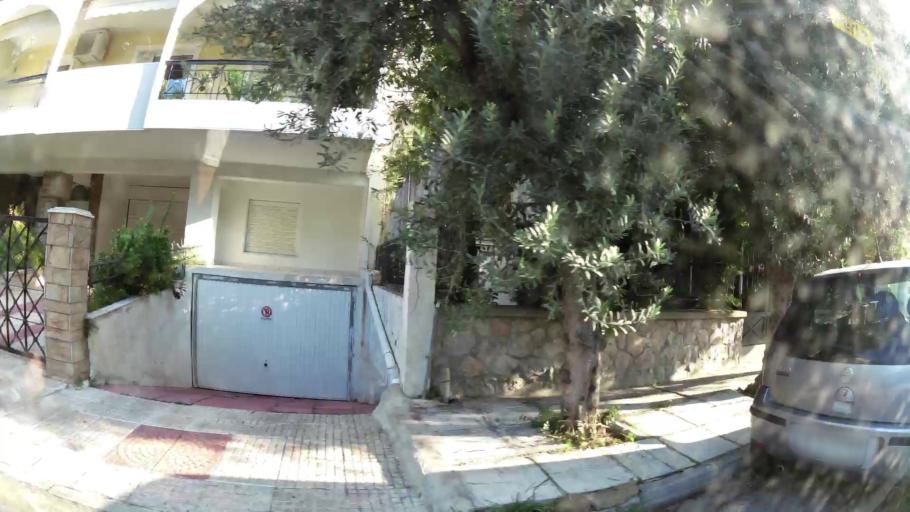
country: GR
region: Attica
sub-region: Nomarchia Athinas
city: Kaisariani
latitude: 37.9699
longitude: 23.7682
